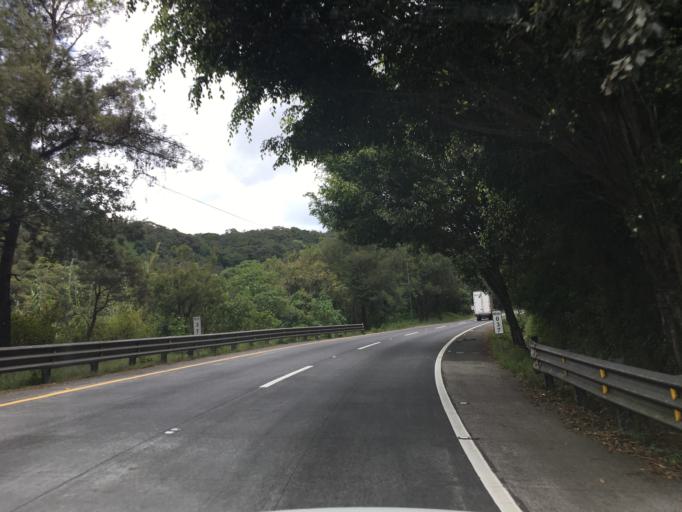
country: GT
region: Sacatepequez
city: Santa Lucia Milpas Altas
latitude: 14.5665
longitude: -90.6874
